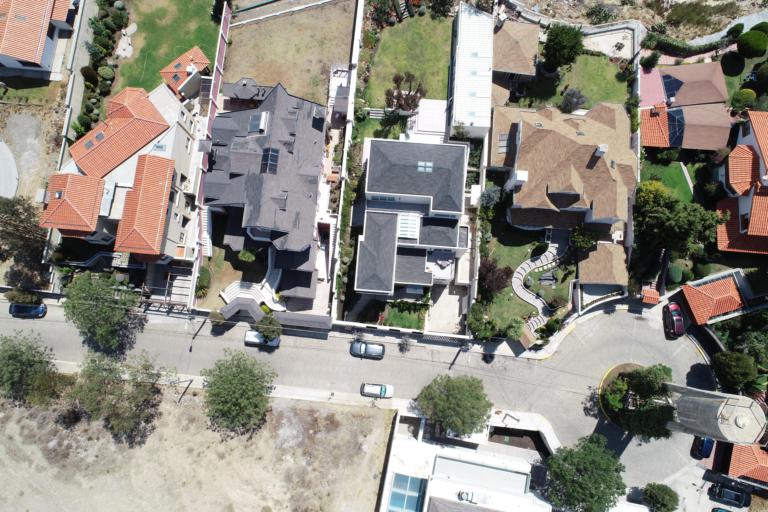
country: BO
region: La Paz
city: La Paz
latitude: -16.5296
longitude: -68.0916
